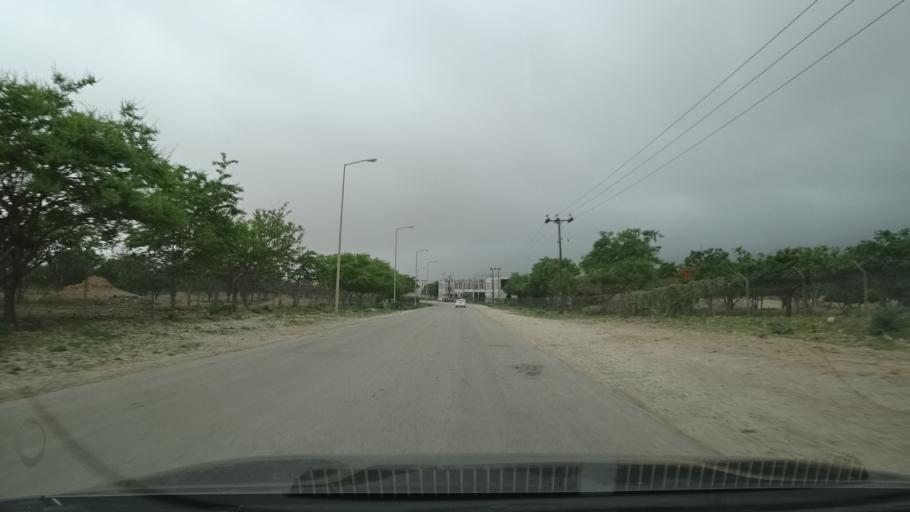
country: OM
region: Zufar
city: Salalah
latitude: 17.0871
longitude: 54.0745
